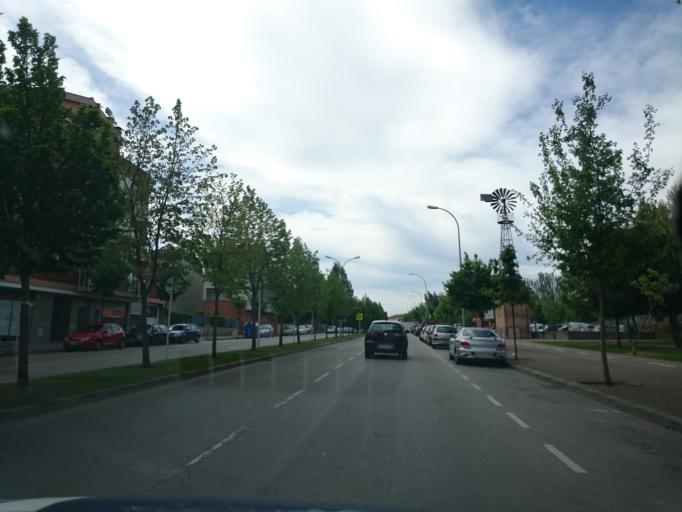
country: ES
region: Catalonia
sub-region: Provincia de Barcelona
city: Vic
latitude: 41.9240
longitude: 2.2487
